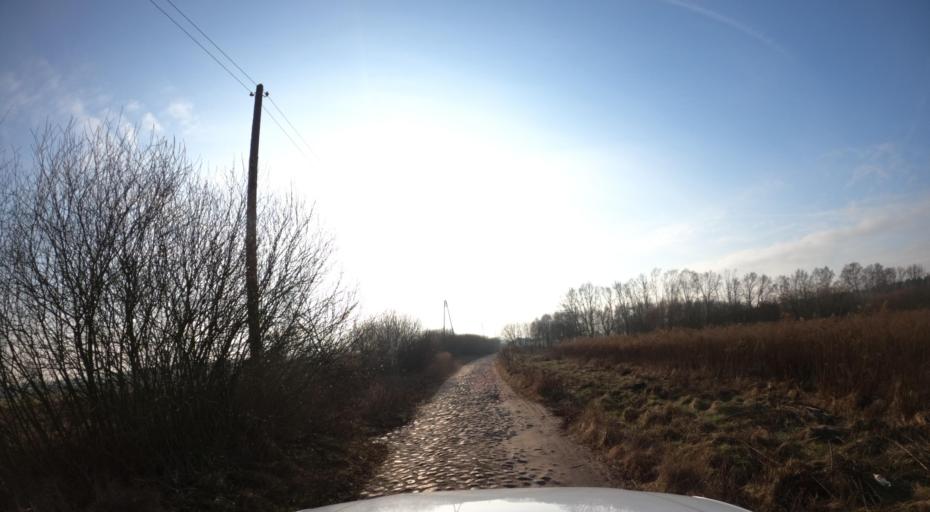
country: PL
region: Lubusz
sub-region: Powiat gorzowski
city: Kostrzyn nad Odra
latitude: 52.6217
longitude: 14.6258
